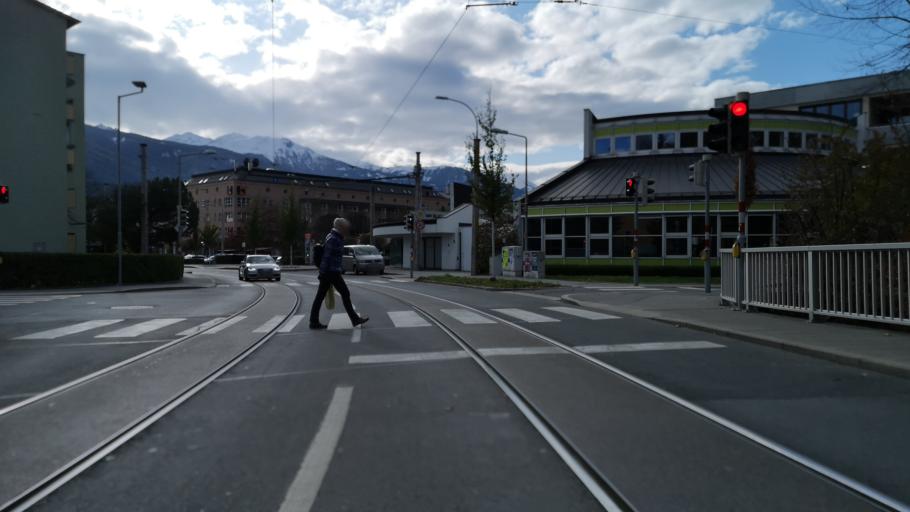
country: AT
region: Tyrol
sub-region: Politischer Bezirk Innsbruck Land
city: Vols
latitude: 47.2673
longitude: 11.3465
